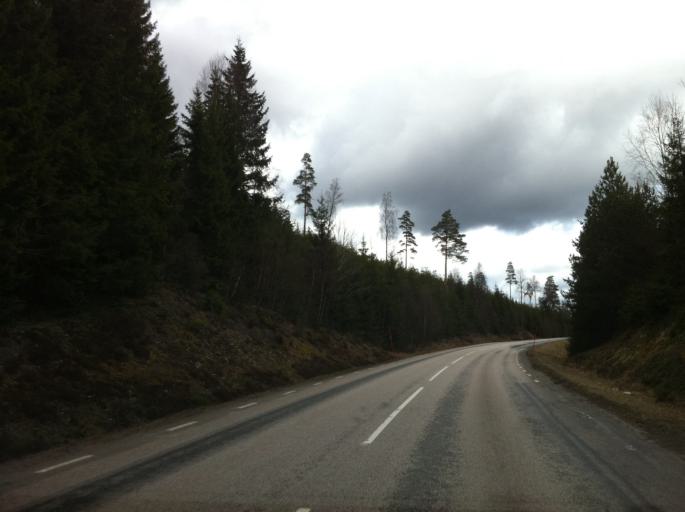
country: SE
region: Joenkoeping
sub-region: Gislaveds Kommun
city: Smalandsstenar
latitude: 57.2623
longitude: 13.2423
